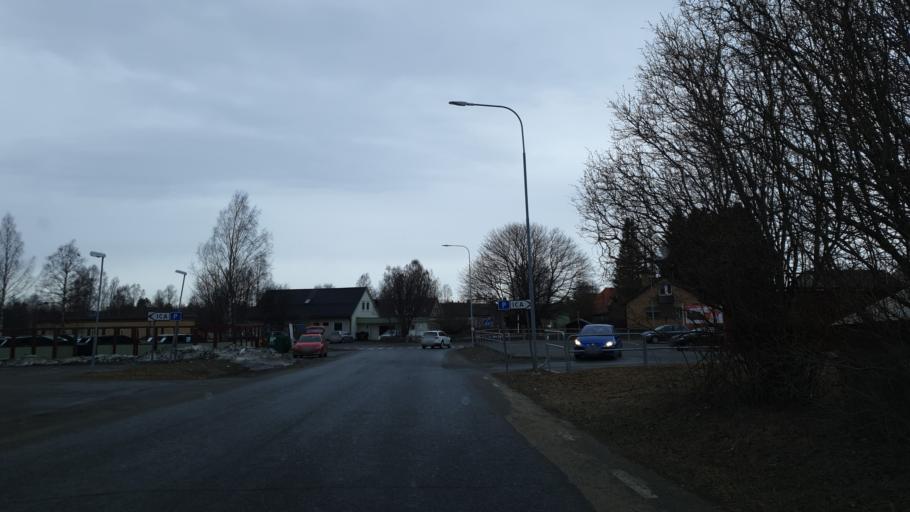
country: SE
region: Vaesterbotten
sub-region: Skelleftea Kommun
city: Kage
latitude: 64.8317
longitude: 20.9874
